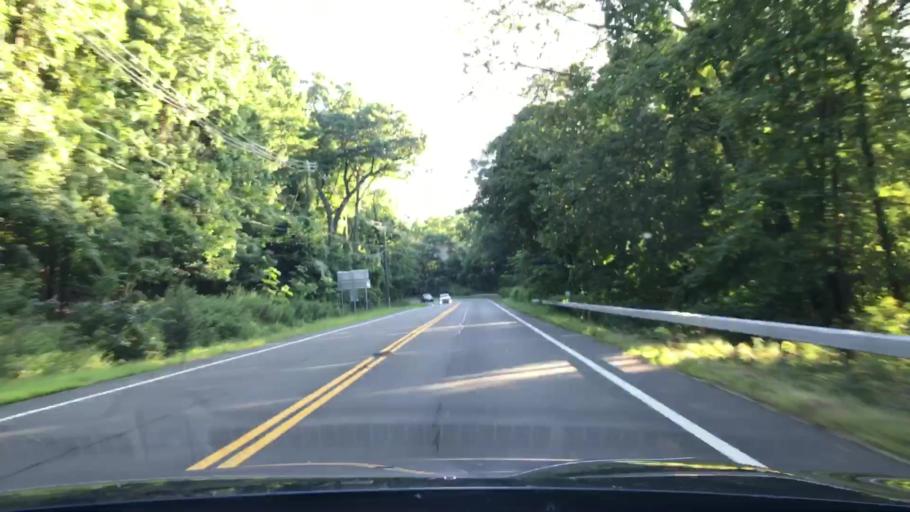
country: US
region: New York
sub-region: Rockland County
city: Sparkill
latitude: 41.0068
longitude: -73.9151
